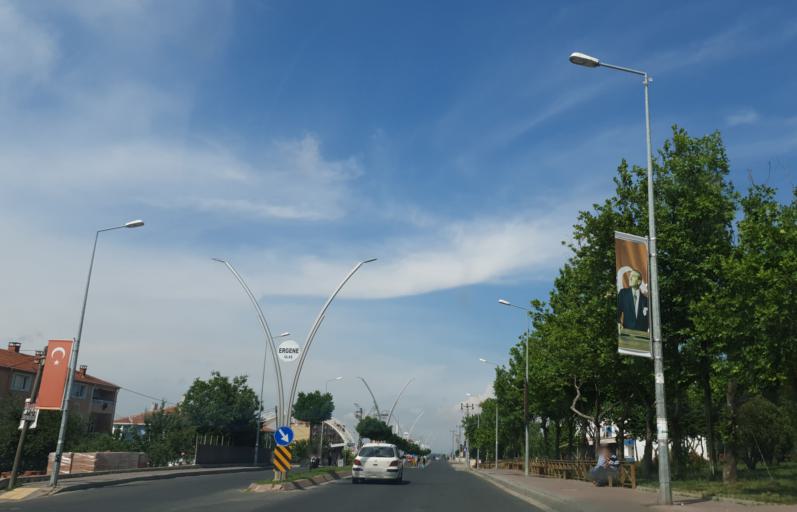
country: TR
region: Tekirdag
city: Marmaracik
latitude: 41.2382
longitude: 27.7105
